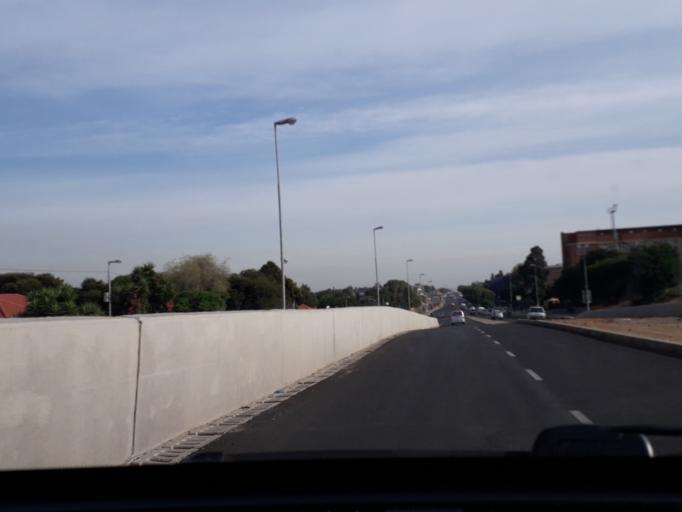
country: ZA
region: Gauteng
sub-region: City of Johannesburg Metropolitan Municipality
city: Johannesburg
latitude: -26.1375
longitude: 28.0864
